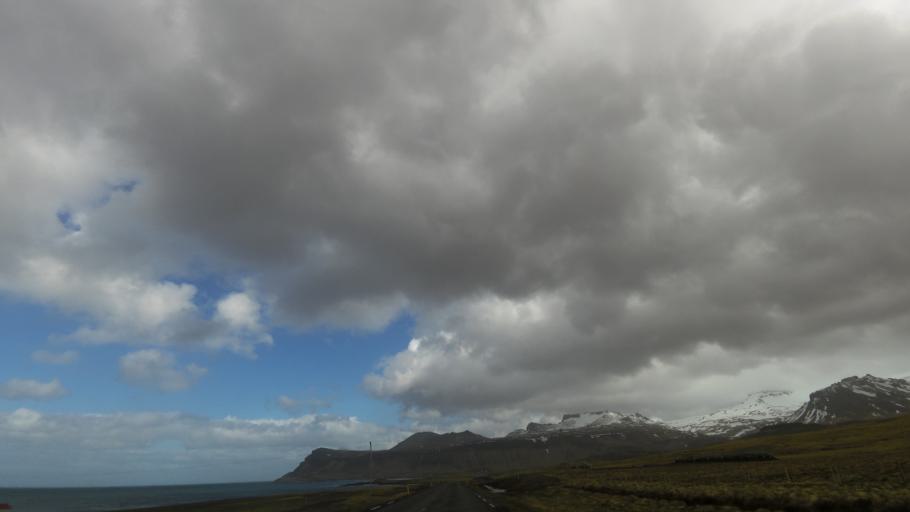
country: IS
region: West
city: Olafsvik
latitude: 64.9070
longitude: -23.5662
